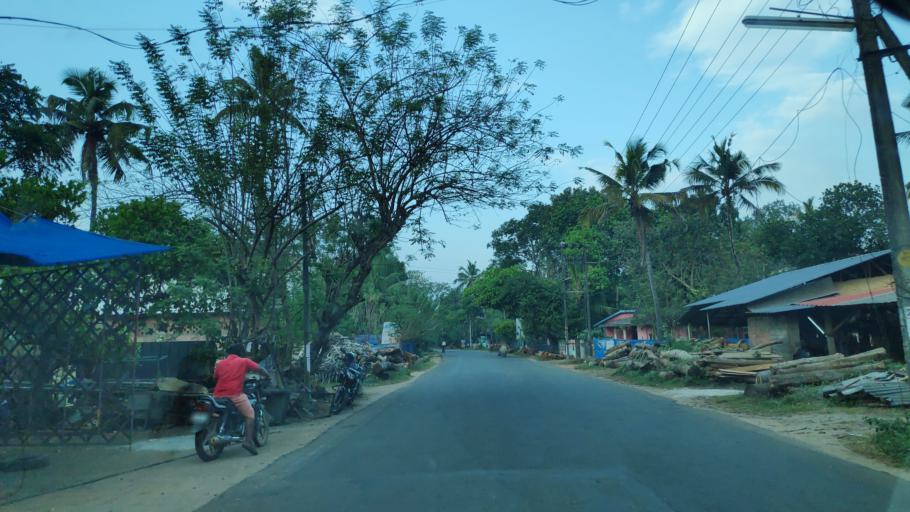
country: IN
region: Kerala
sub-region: Alappuzha
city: Shertallai
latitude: 9.6362
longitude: 76.3717
